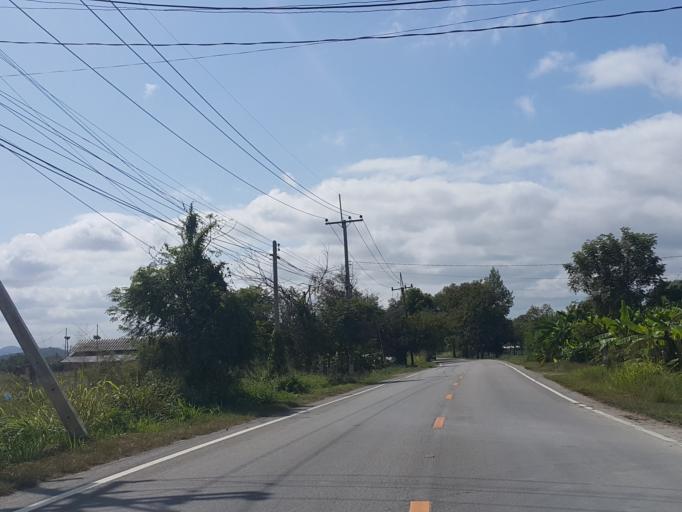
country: TH
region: Chiang Mai
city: San Kamphaeng
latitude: 18.7108
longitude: 99.1689
